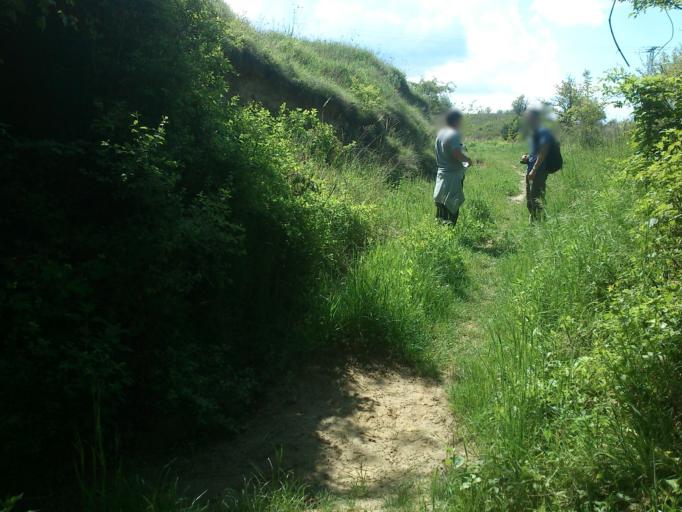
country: HU
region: Komarom-Esztergom
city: Kesztolc
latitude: 47.7094
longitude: 18.7907
